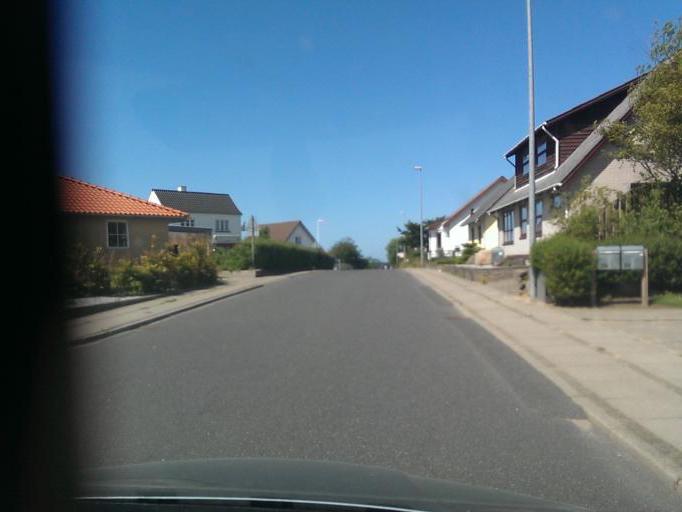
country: DK
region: North Denmark
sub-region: Jammerbugt Kommune
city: Pandrup
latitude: 57.3133
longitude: 9.7142
